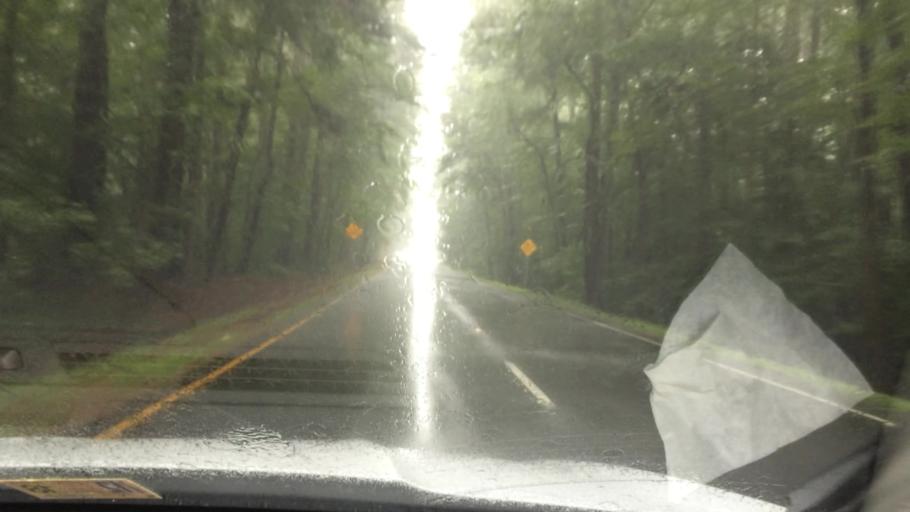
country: US
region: Virginia
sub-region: James City County
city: Williamsburg
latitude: 37.3931
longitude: -76.7755
